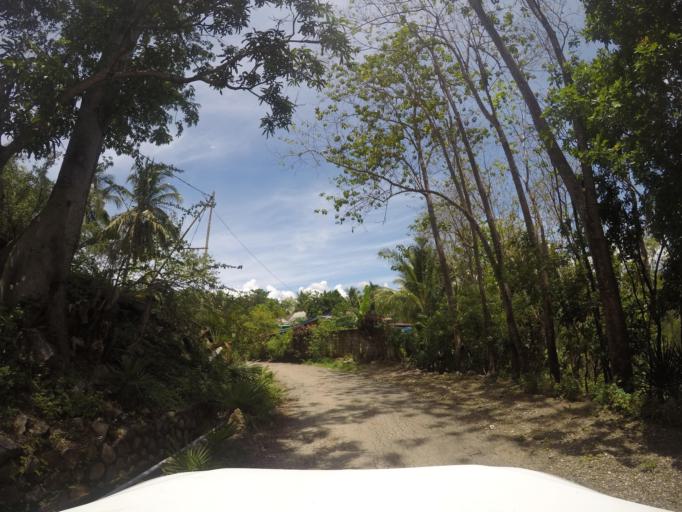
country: TL
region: Bobonaro
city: Maliana
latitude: -8.9971
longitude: 125.2224
